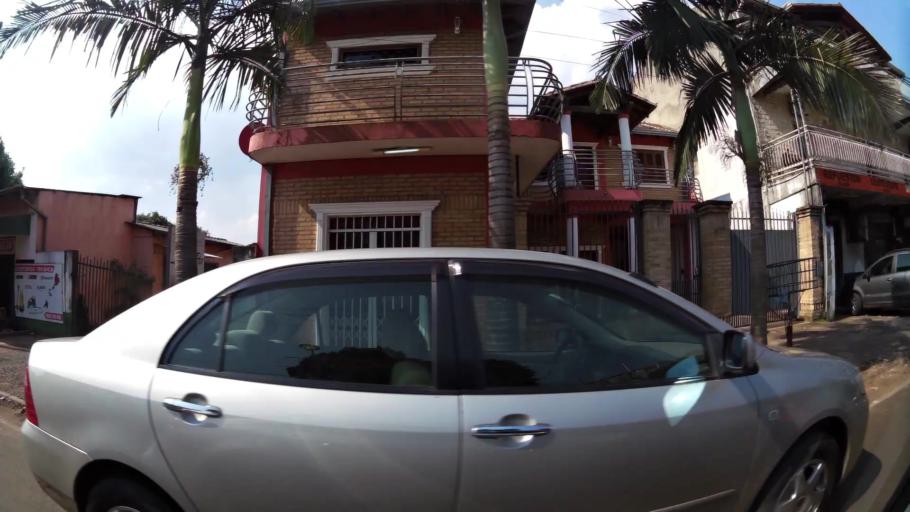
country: PY
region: Alto Parana
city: Ciudad del Este
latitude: -25.5069
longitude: -54.6343
